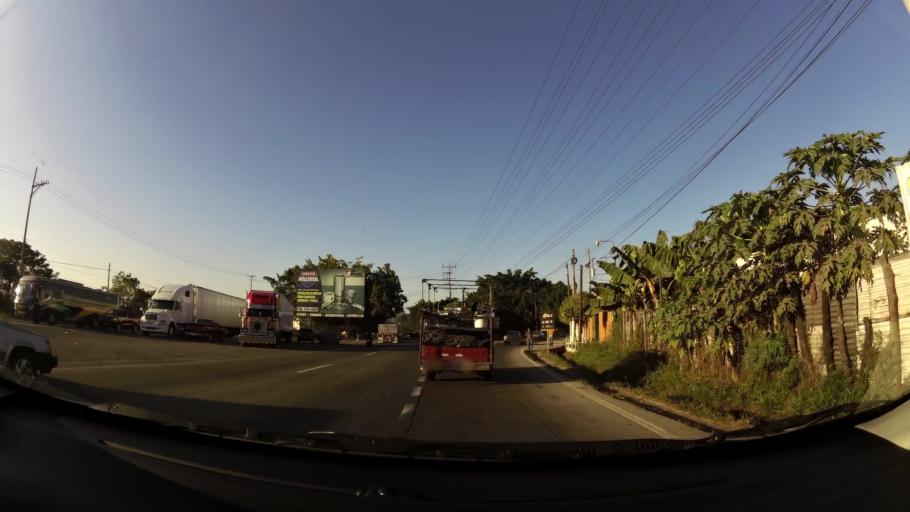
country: SV
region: La Libertad
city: Ciudad Arce
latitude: 13.7772
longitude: -89.3729
